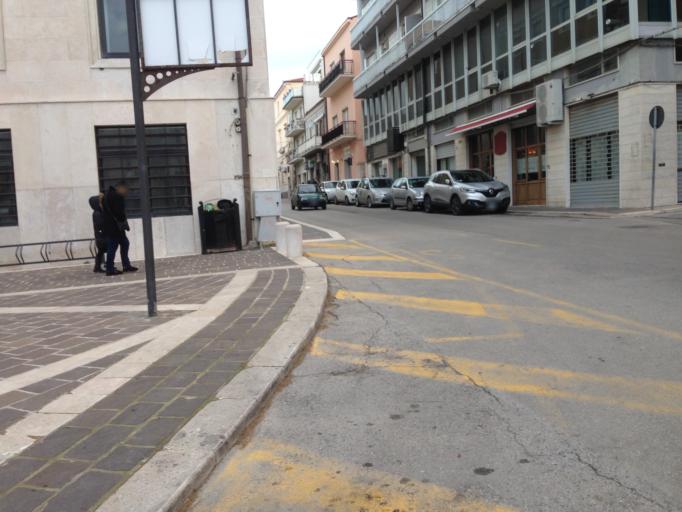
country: IT
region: Molise
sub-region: Provincia di Campobasso
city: Termoli
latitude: 42.0028
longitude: 14.9944
